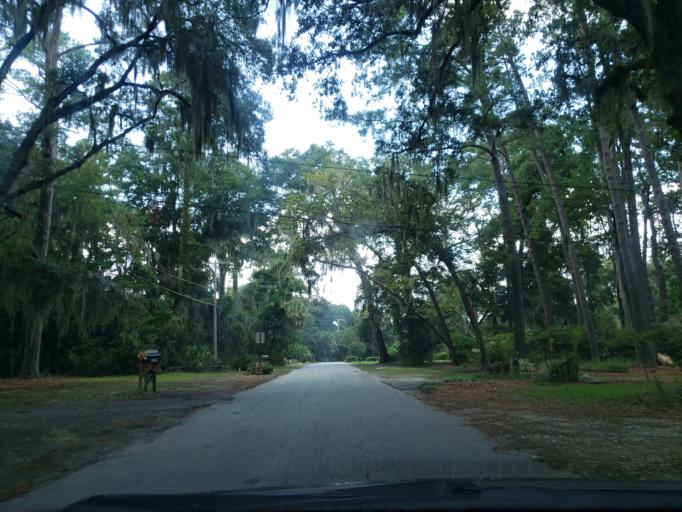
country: US
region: Georgia
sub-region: Chatham County
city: Montgomery
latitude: 31.9299
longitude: -81.0982
